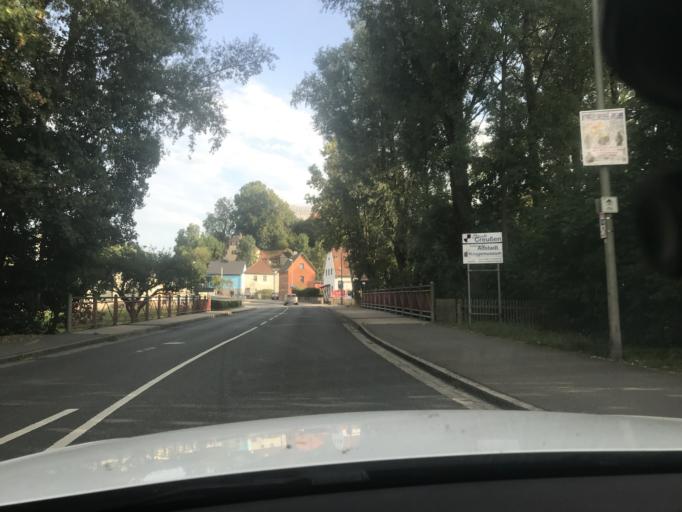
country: DE
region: Bavaria
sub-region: Upper Franconia
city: Creussen
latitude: 49.8468
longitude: 11.6228
